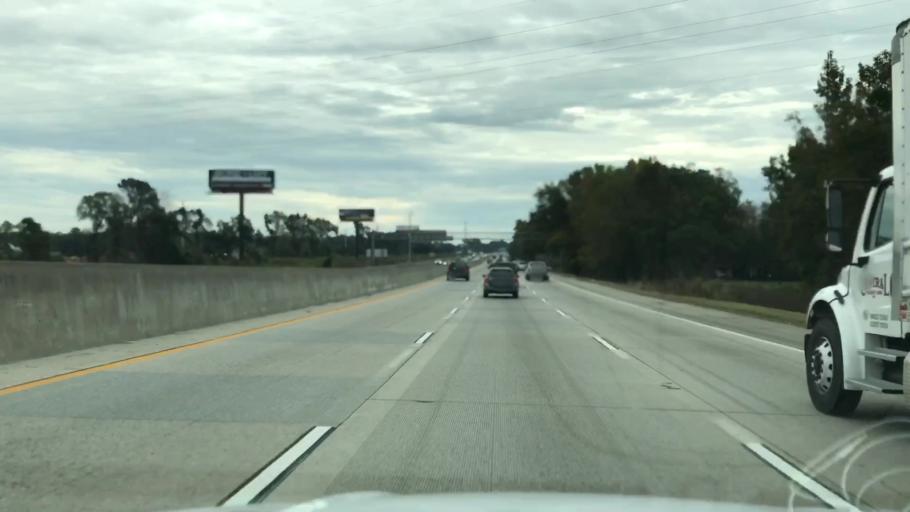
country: US
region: South Carolina
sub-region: Charleston County
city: North Charleston
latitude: 32.8632
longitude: -79.9963
